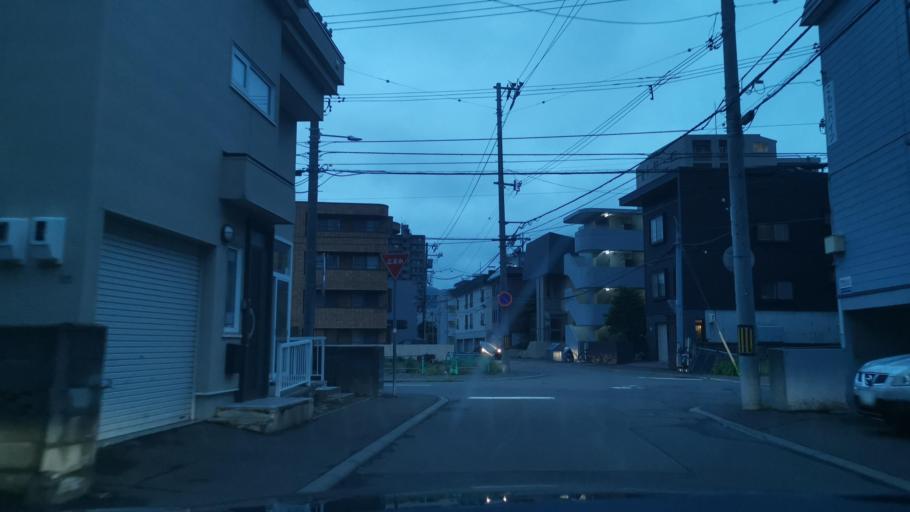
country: JP
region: Hokkaido
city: Sapporo
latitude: 43.0631
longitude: 141.3122
